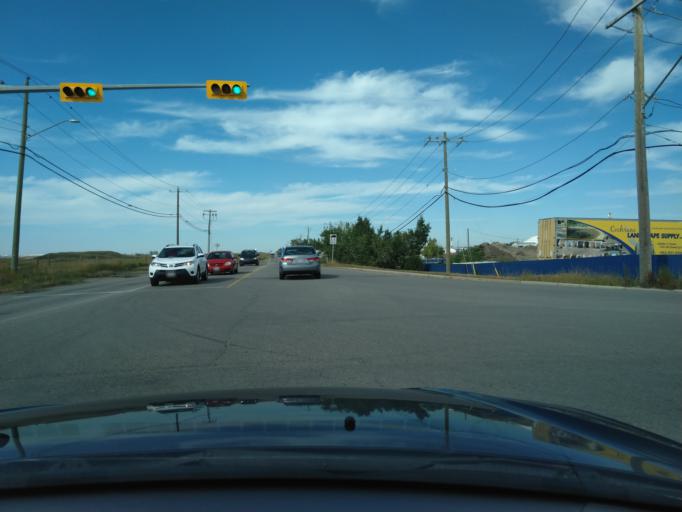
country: CA
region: Alberta
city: Calgary
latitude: 51.1132
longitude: -113.9818
